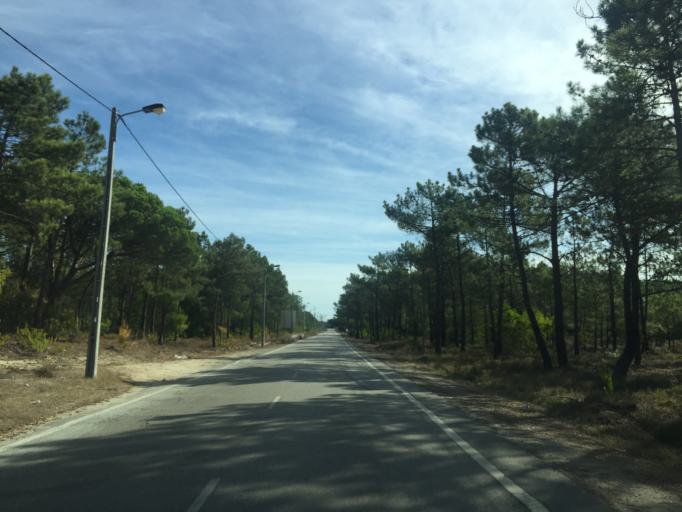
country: PT
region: Coimbra
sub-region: Figueira da Foz
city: Lavos
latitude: 40.0901
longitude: -8.8515
